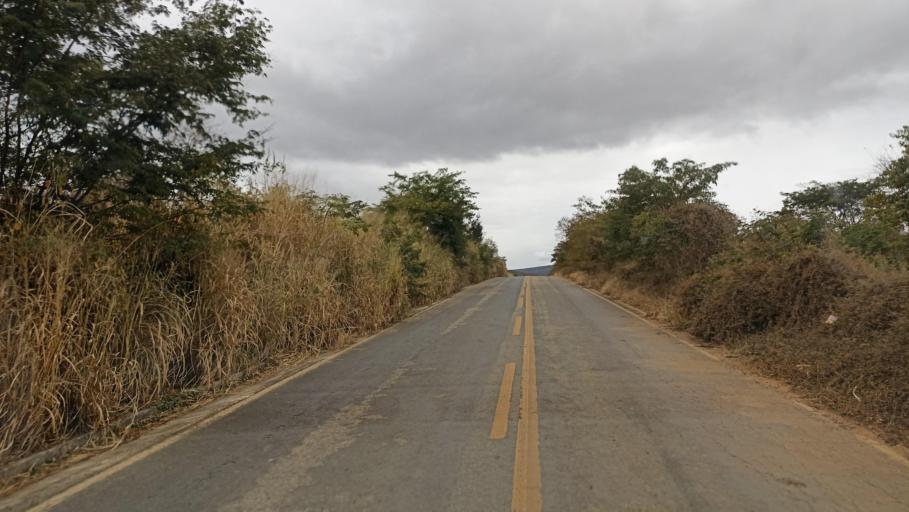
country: BR
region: Minas Gerais
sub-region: Itinga
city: Itinga
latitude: -16.6543
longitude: -41.8313
